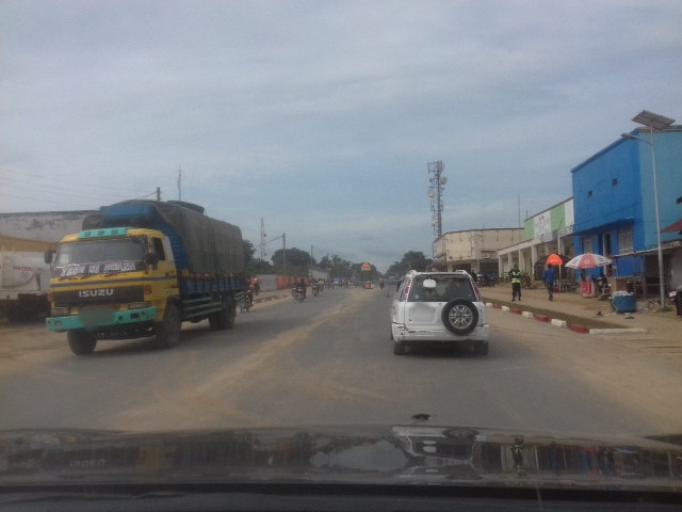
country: CD
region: Eastern Province
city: Bunia
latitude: 1.5561
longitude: 30.2479
